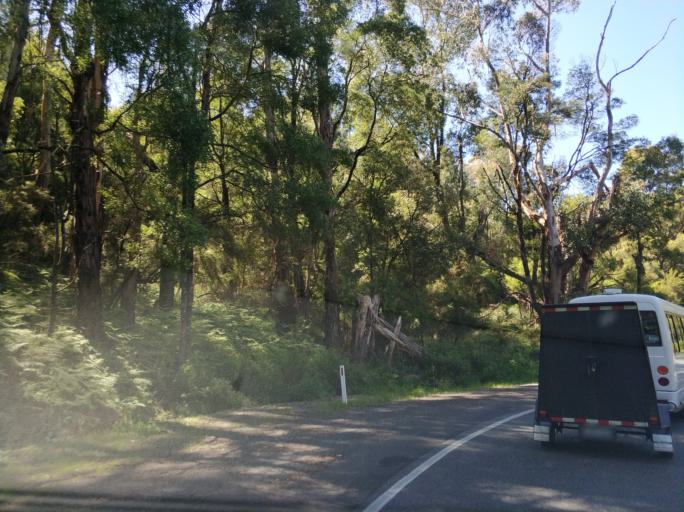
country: AU
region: Victoria
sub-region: Colac-Otway
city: Apollo Bay
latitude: -38.7357
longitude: 143.2509
